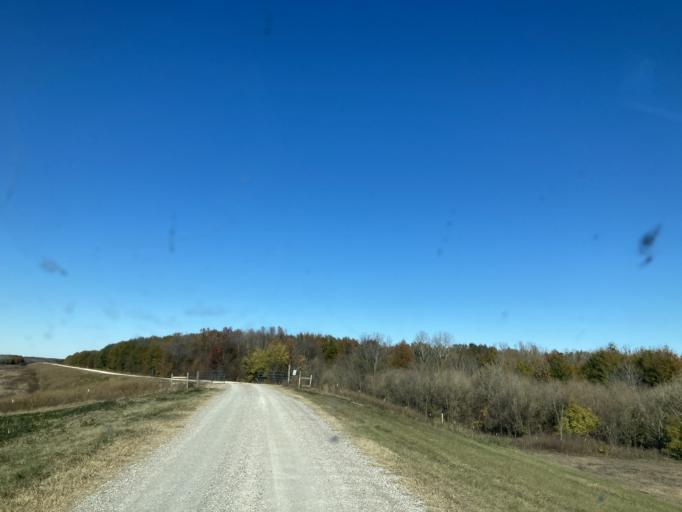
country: US
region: Mississippi
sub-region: Sharkey County
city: Rolling Fork
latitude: 32.7026
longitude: -90.6808
